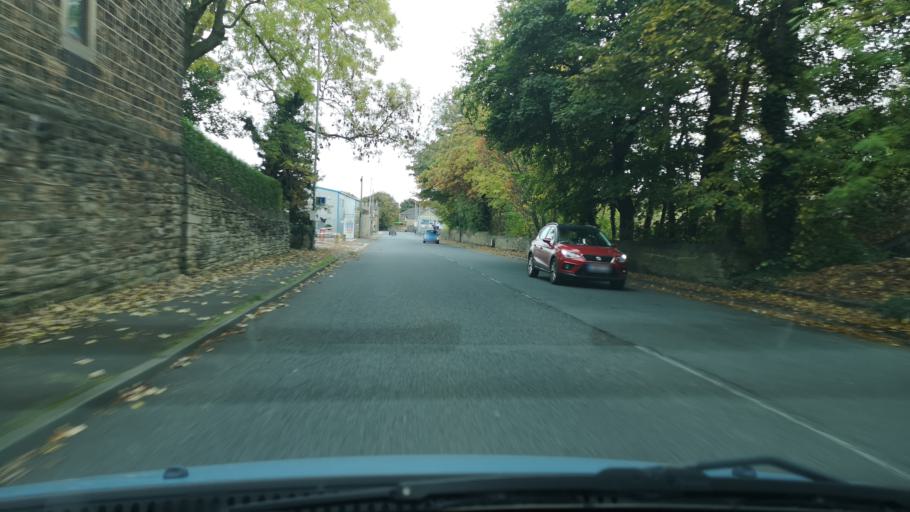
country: GB
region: England
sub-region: Kirklees
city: Heckmondwike
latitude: 53.7234
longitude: -1.6838
